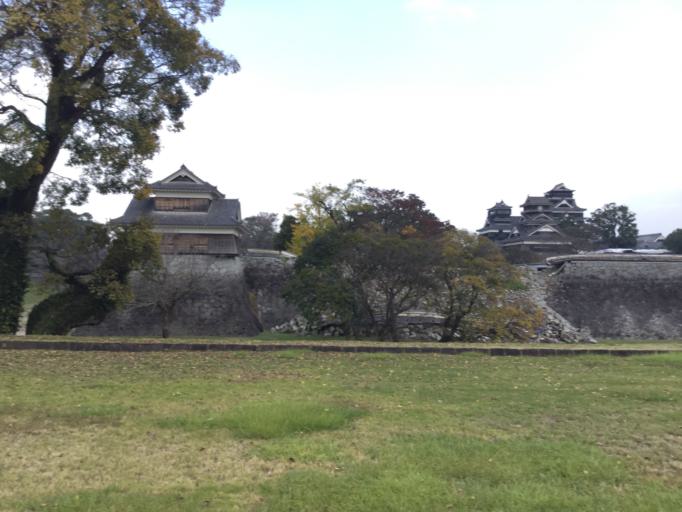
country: JP
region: Kumamoto
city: Kumamoto
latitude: 32.8073
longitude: 130.7027
